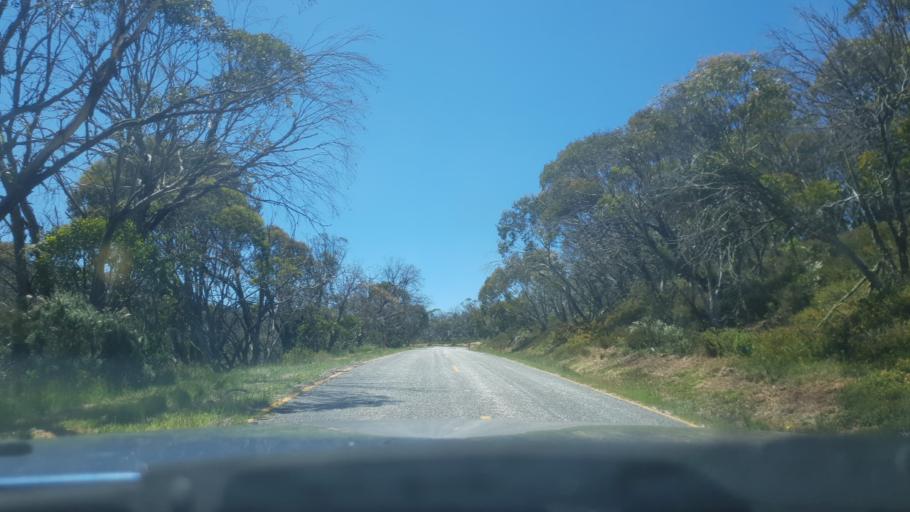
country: AU
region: Victoria
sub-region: Alpine
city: Mount Beauty
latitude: -36.9353
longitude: 147.3083
